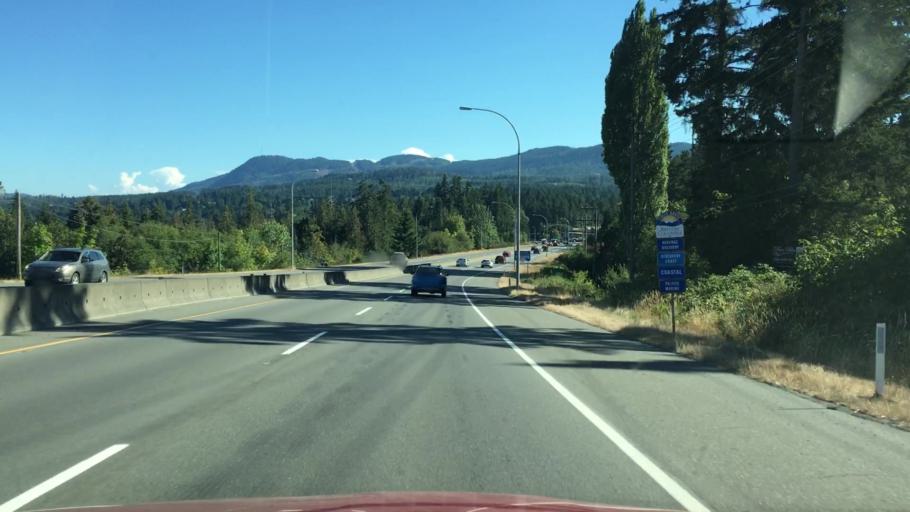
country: CA
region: British Columbia
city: North Saanich
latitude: 48.6627
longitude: -123.5596
